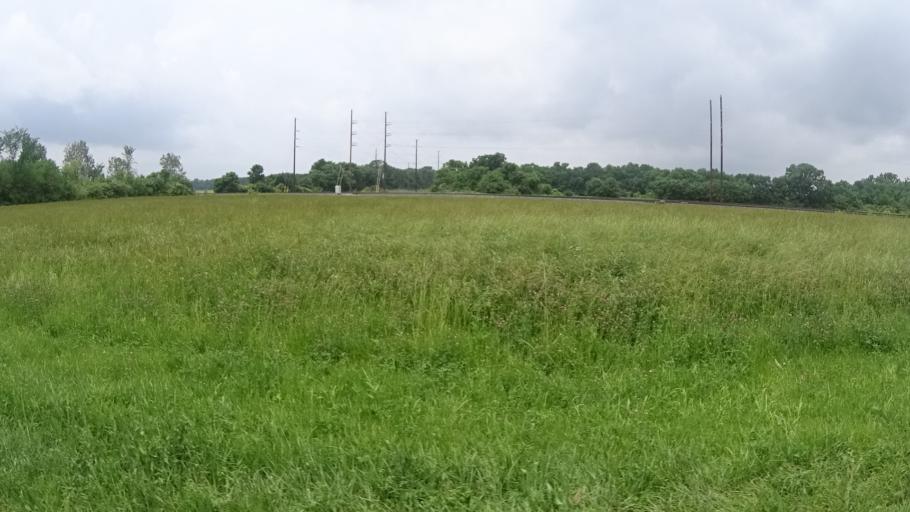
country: US
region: Ohio
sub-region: Huron County
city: Bellevue
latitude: 41.3322
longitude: -82.7935
